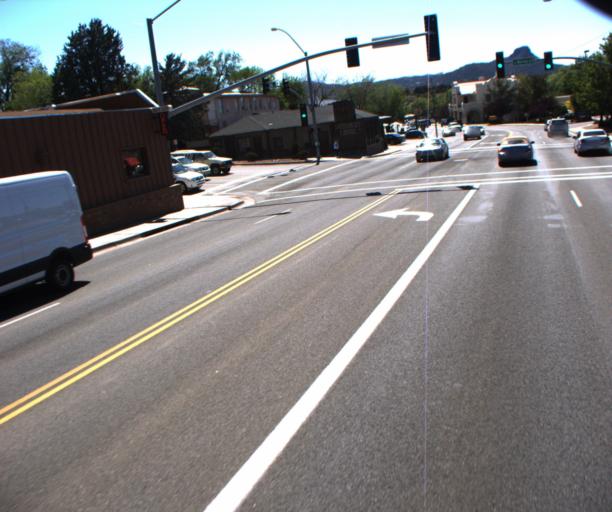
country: US
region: Arizona
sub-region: Yavapai County
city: Prescott
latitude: 34.5454
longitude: -112.4668
